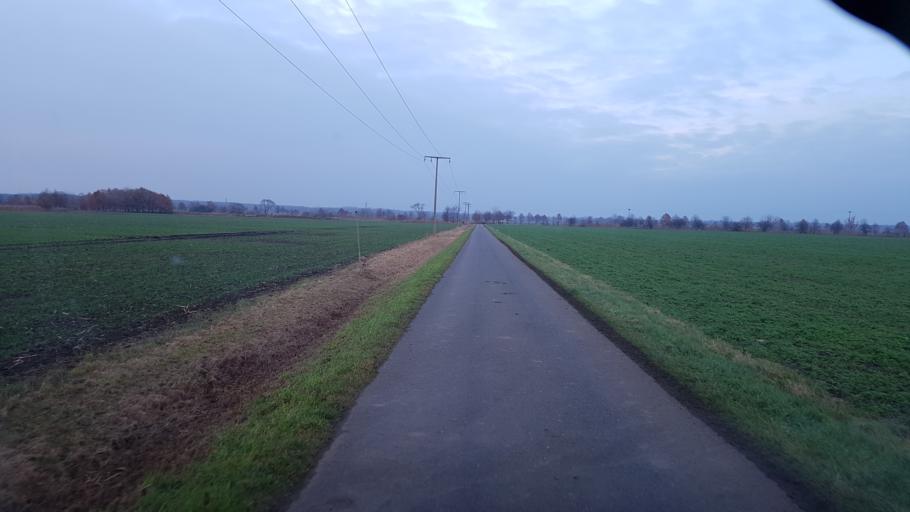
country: DE
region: Brandenburg
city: Ziltendorf
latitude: 52.2373
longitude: 14.6573
